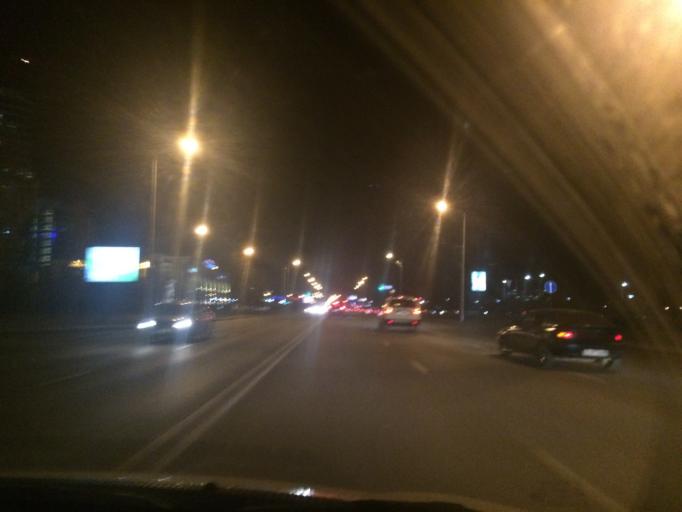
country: KZ
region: Astana Qalasy
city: Astana
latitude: 51.1313
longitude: 71.4063
